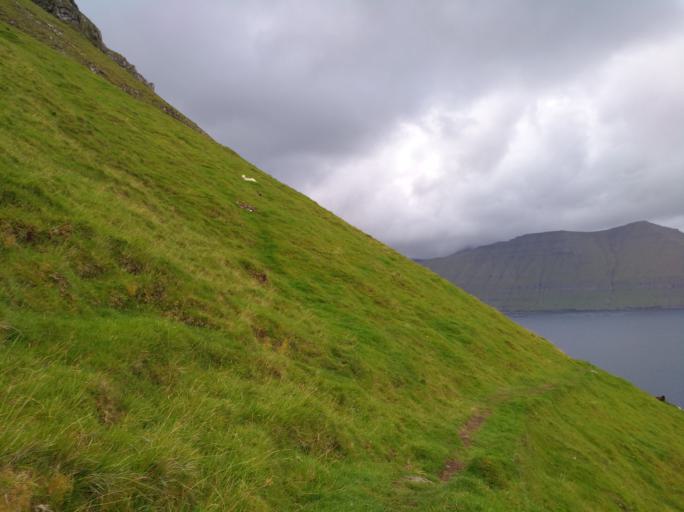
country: FO
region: Eysturoy
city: Fuglafjordur
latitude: 62.2878
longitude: -6.8777
